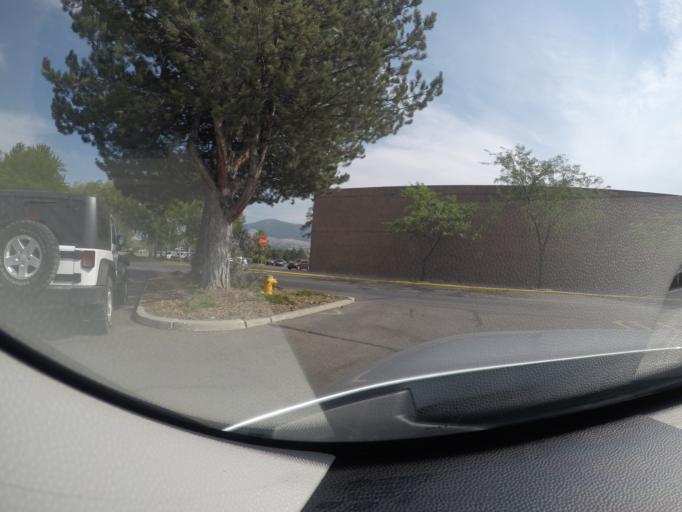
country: US
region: Montana
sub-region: Missoula County
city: Orchard Homes
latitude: 46.8479
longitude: -114.0268
